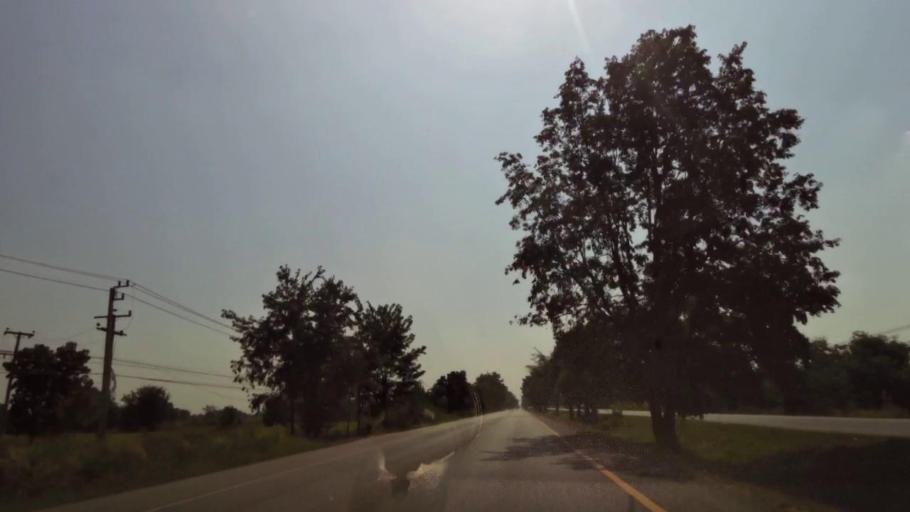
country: TH
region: Phichit
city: Bueng Na Rang
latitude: 16.2874
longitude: 100.1277
